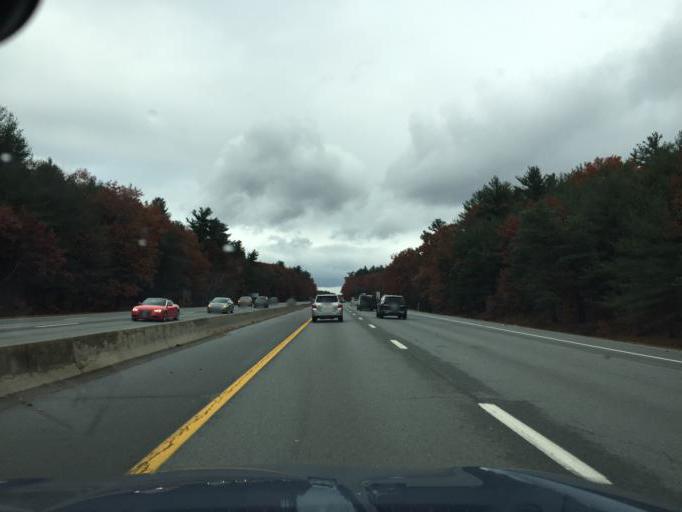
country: US
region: New Hampshire
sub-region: Hillsborough County
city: Nashua
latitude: 42.7934
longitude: -71.4965
